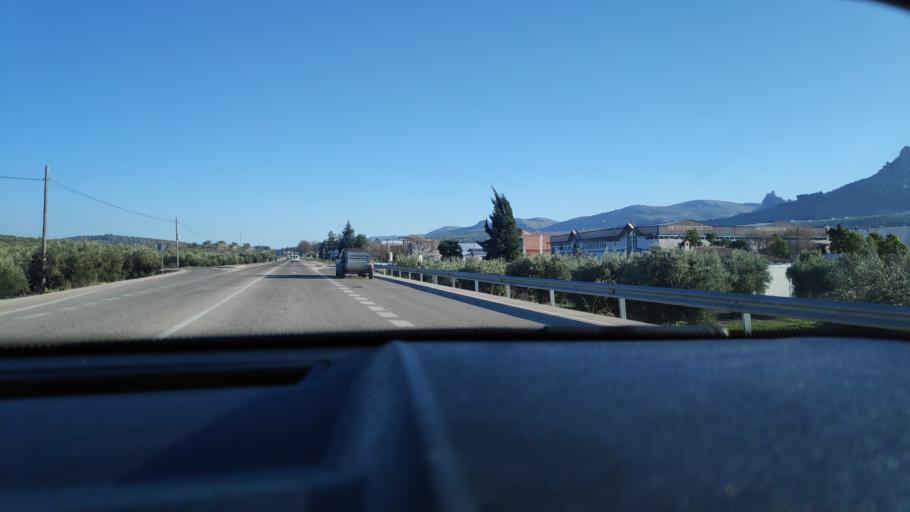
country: ES
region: Andalusia
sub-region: Province of Cordoba
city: Luque
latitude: 37.5824
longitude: -4.2861
